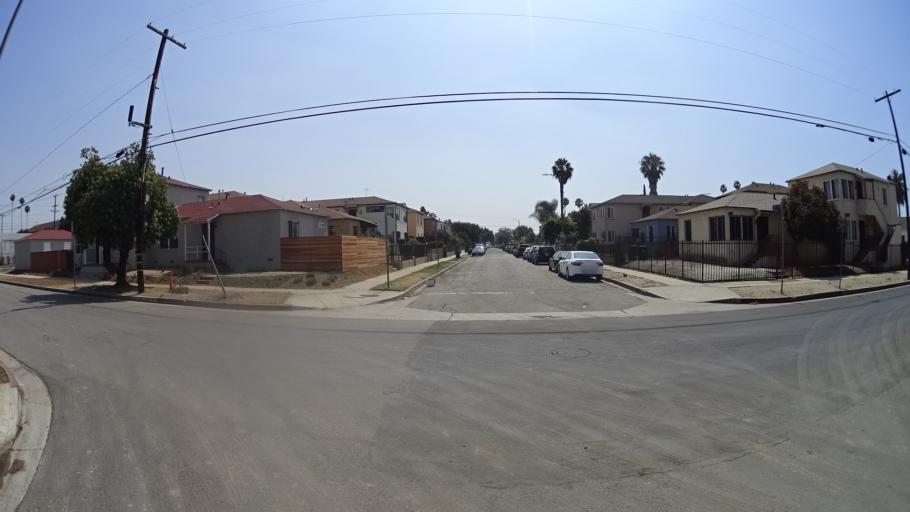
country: US
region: California
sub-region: Los Angeles County
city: View Park-Windsor Hills
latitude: 34.0246
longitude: -118.3157
